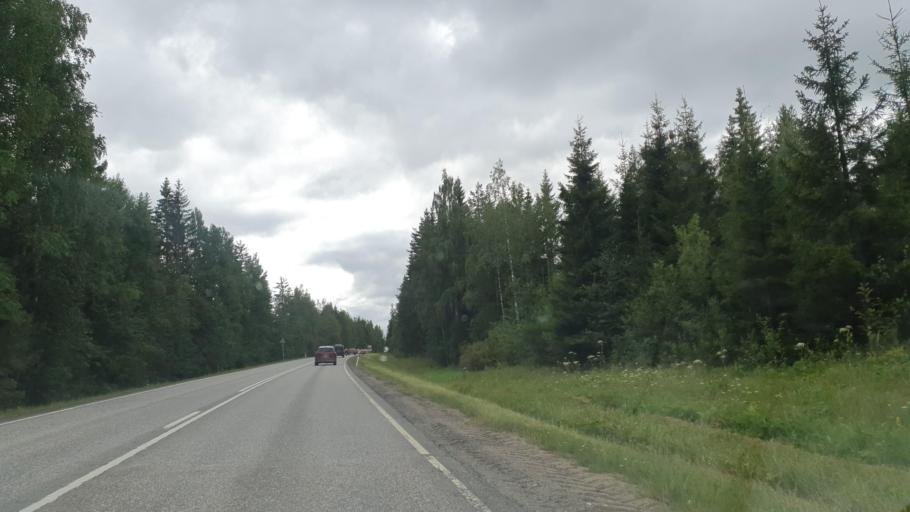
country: FI
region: Northern Savo
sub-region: Ylae-Savo
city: Sonkajaervi
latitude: 63.6853
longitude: 27.3399
